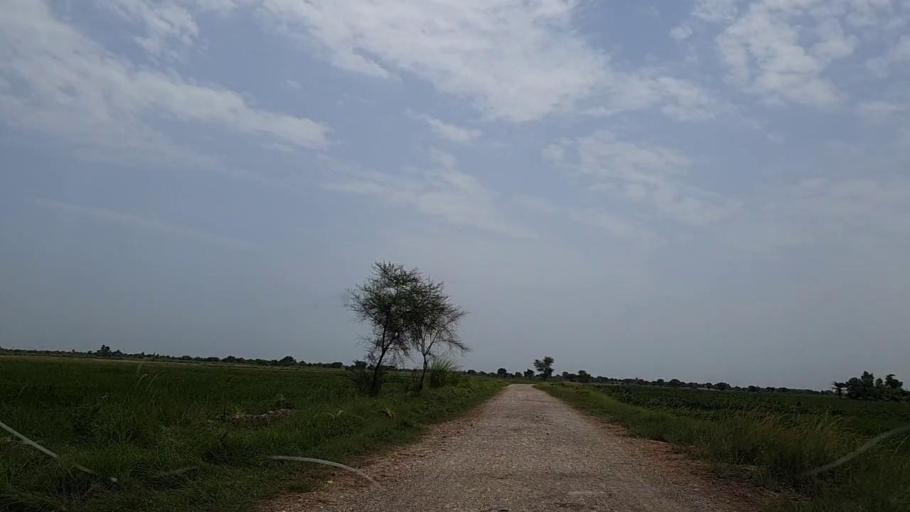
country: PK
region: Sindh
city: Tharu Shah
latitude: 26.9154
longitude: 68.0809
